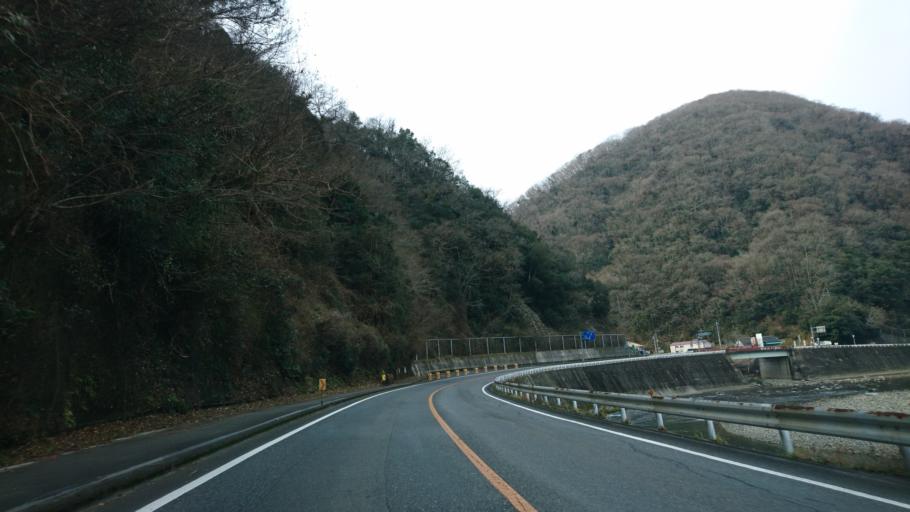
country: JP
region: Okayama
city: Takahashi
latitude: 34.8539
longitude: 133.5715
